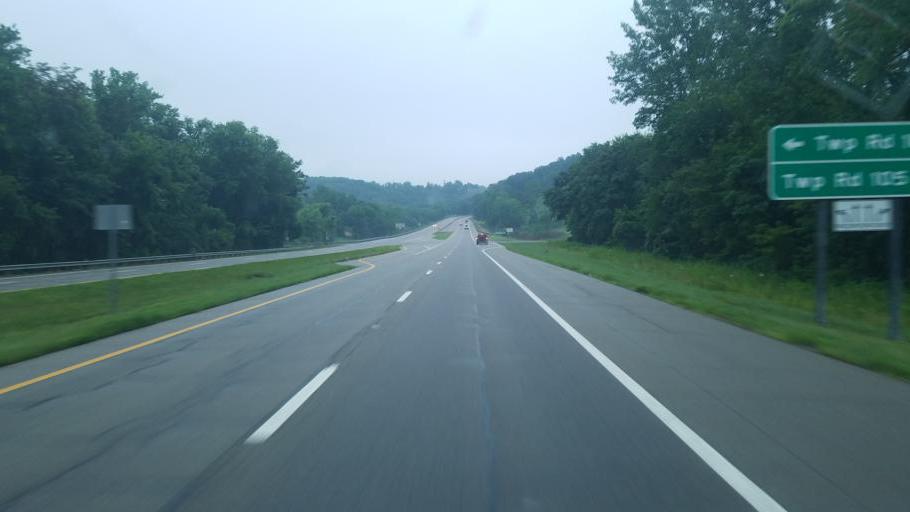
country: US
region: Ohio
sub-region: Tuscarawas County
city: Newcomerstown
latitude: 40.2825
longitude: -81.6423
